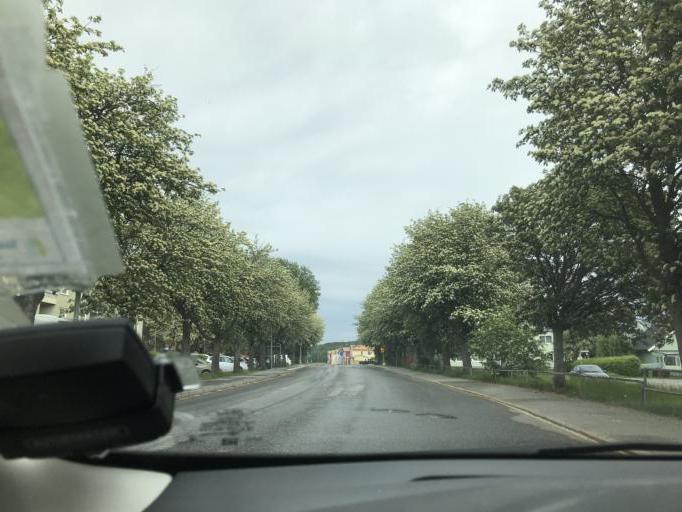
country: SE
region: Stockholm
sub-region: Botkyrka Kommun
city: Tumba
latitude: 59.2041
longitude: 17.8341
